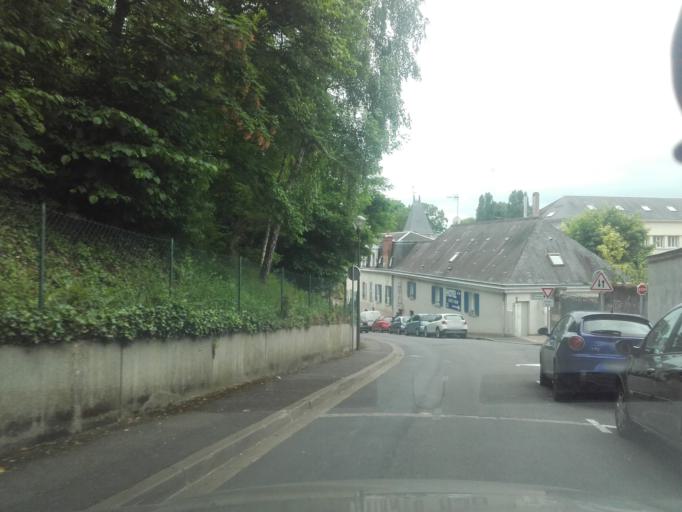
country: FR
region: Centre
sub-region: Departement d'Indre-et-Loire
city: Tours
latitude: 47.4029
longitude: 0.6867
